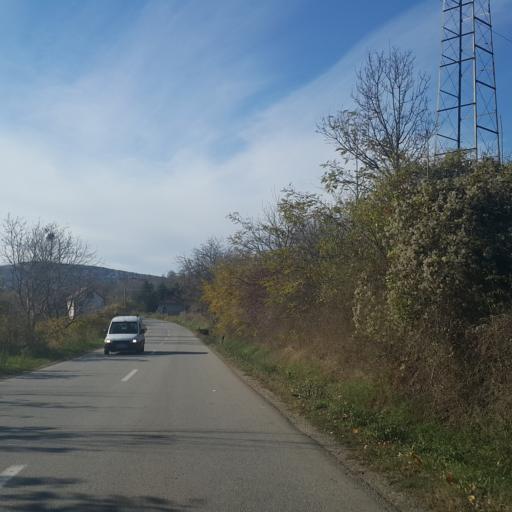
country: RS
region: Central Serbia
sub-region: Sumadijski Okrug
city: Topola
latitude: 44.2499
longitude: 20.7195
